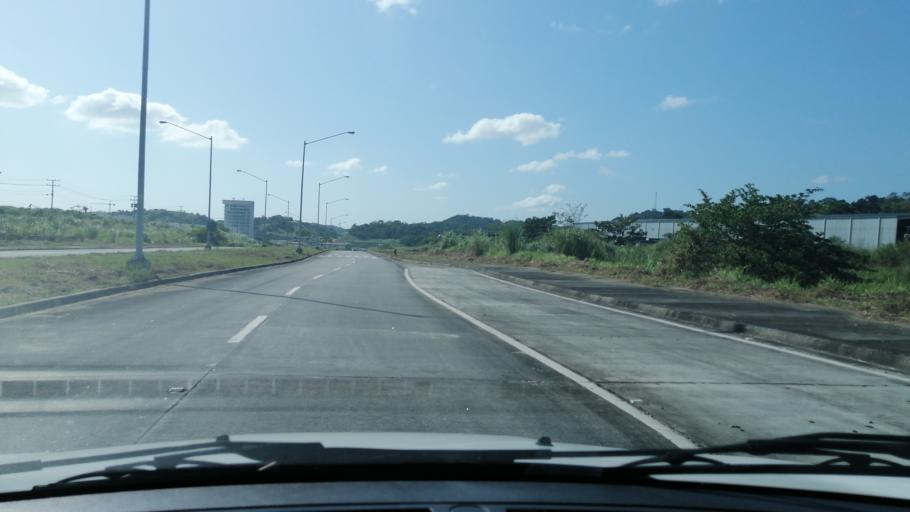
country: PA
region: Panama
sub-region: Distrito de Panama
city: Paraiso
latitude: 9.0298
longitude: -79.5816
